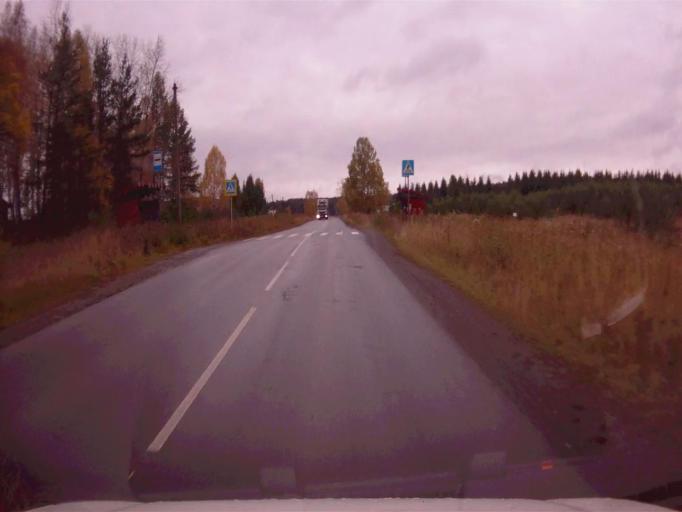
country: RU
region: Chelyabinsk
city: Verkhniy Ufaley
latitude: 56.0591
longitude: 60.1809
